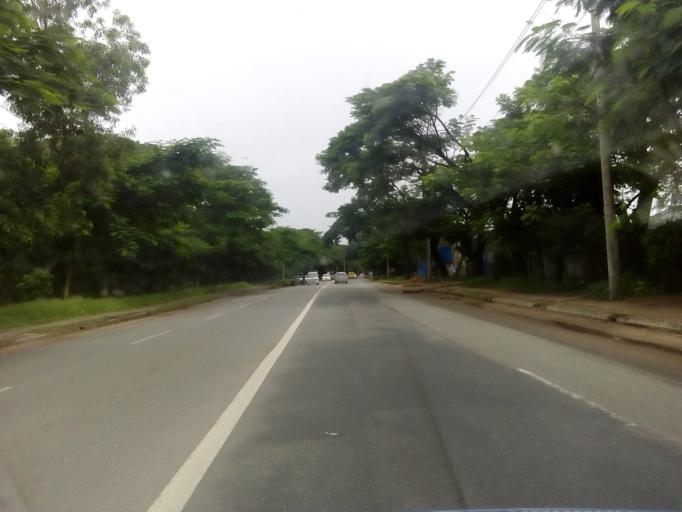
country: MM
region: Yangon
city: Yangon
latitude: 16.8556
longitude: 96.1349
